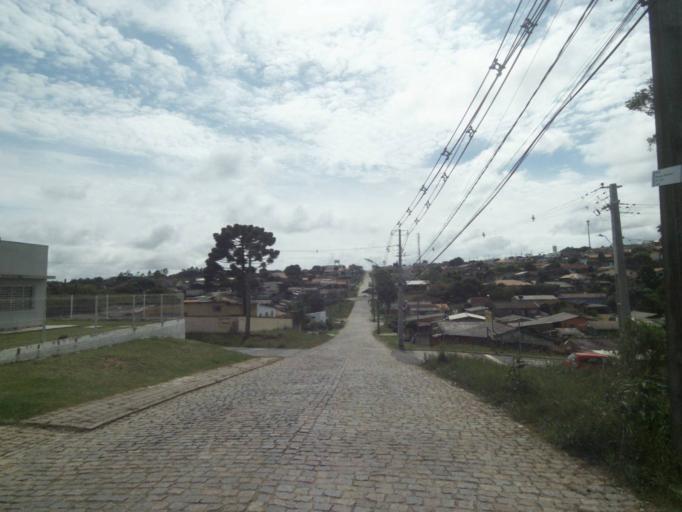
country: BR
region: Parana
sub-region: Campina Grande Do Sul
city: Campina Grande do Sul
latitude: -25.3094
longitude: -49.0572
